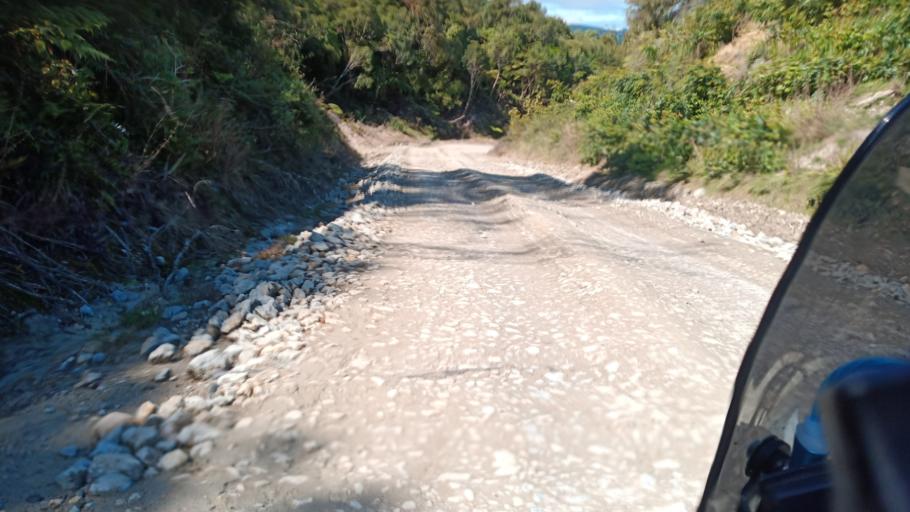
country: NZ
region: Gisborne
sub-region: Gisborne District
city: Gisborne
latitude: -38.8847
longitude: 177.7836
